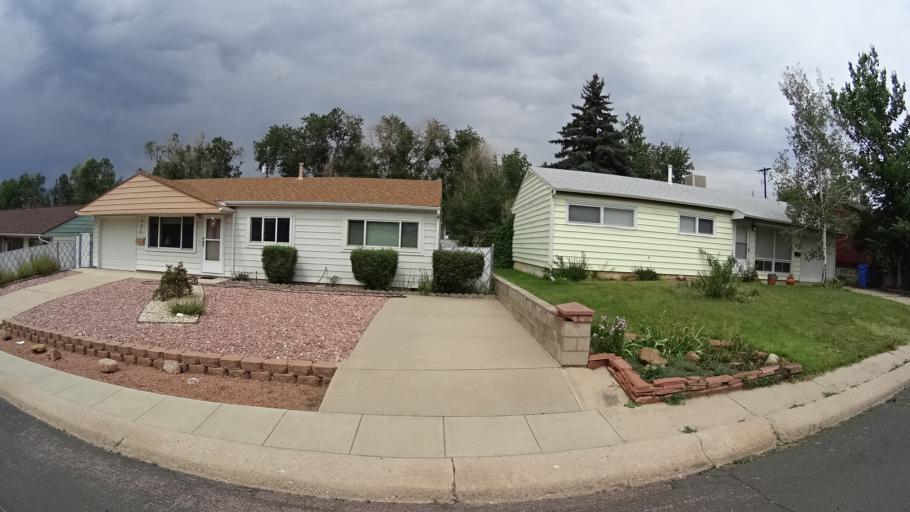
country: US
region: Colorado
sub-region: El Paso County
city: Colorado Springs
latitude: 38.8957
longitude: -104.8133
